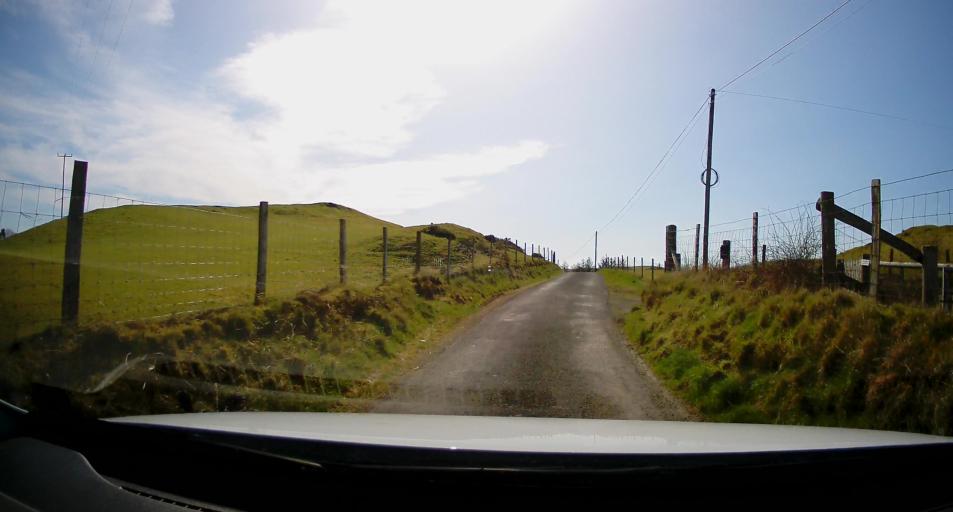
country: GB
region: Wales
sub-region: County of Ceredigion
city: Lledrod
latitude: 52.3601
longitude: -3.8724
